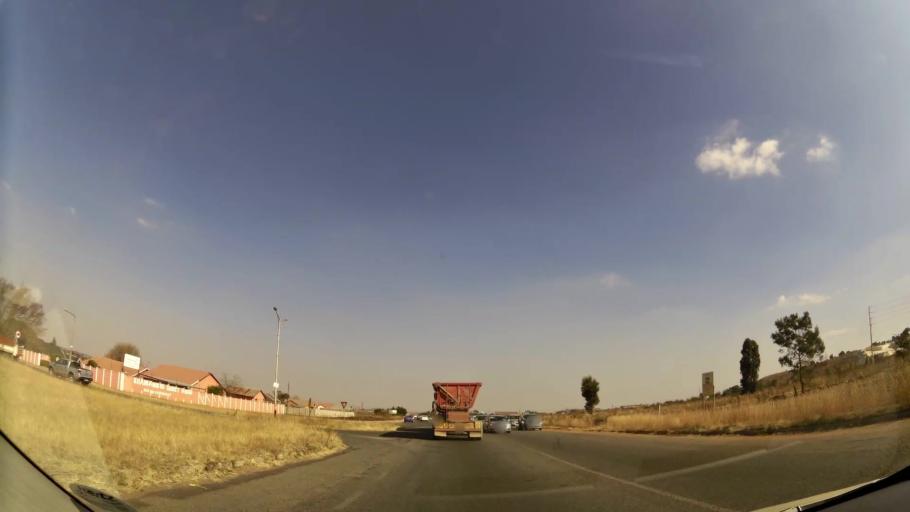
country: ZA
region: Gauteng
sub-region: City of Johannesburg Metropolitan Municipality
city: Roodepoort
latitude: -26.1401
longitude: 27.8172
